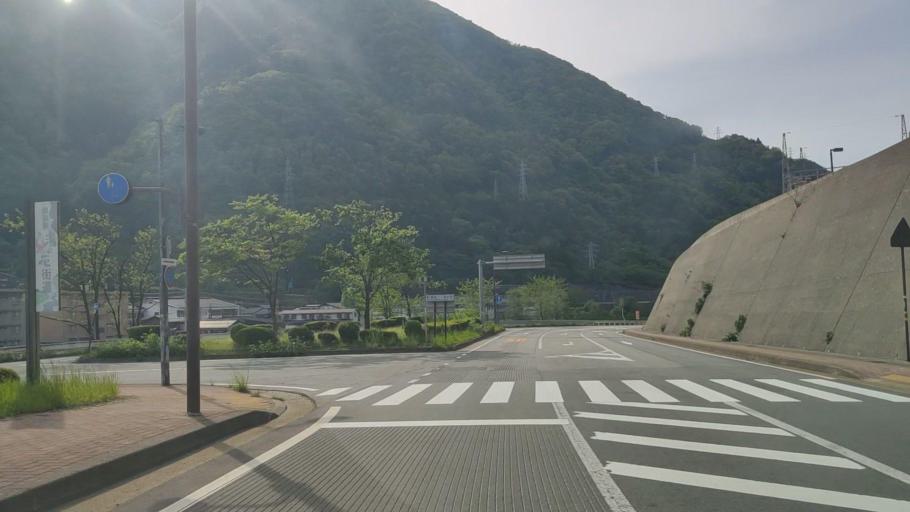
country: JP
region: Gifu
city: Takayama
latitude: 36.3364
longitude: 137.2990
